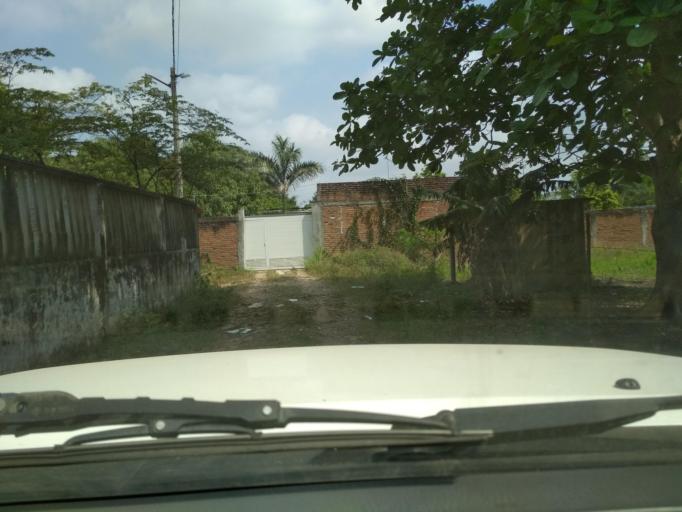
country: MX
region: Veracruz
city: El Tejar
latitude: 19.0804
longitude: -96.1702
